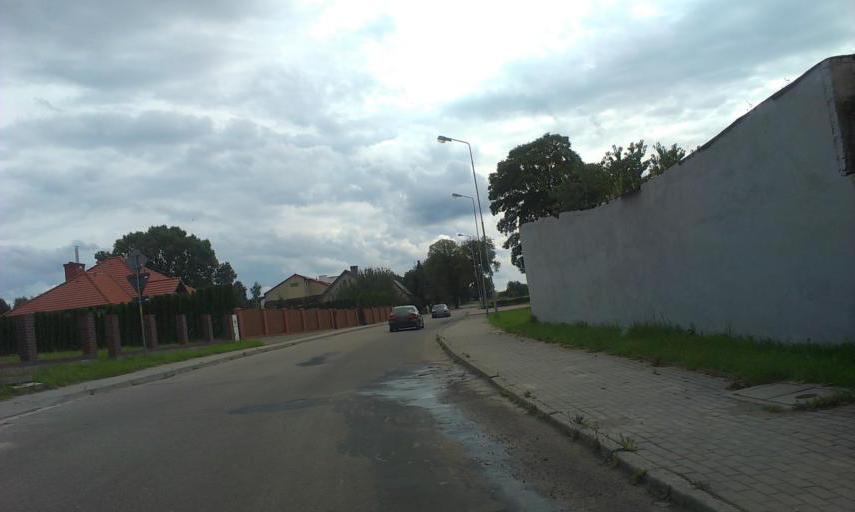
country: PL
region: West Pomeranian Voivodeship
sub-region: Powiat szczecinecki
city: Barwice
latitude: 53.7371
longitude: 16.3549
